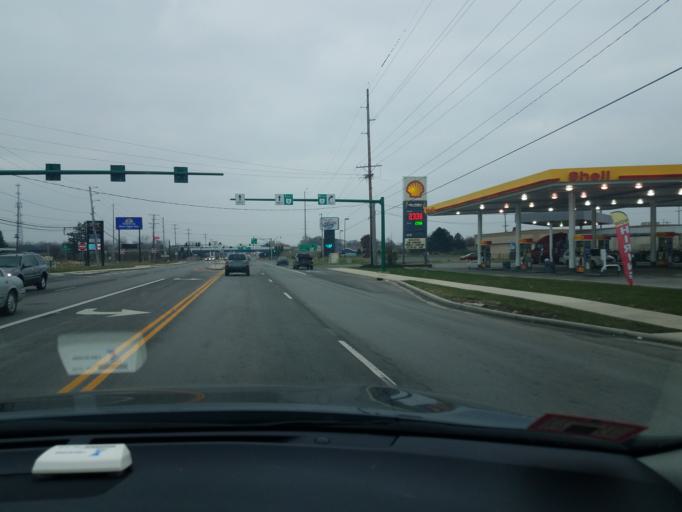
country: US
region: Ohio
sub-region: Erie County
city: Sandusky
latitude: 41.4027
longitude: -82.6585
